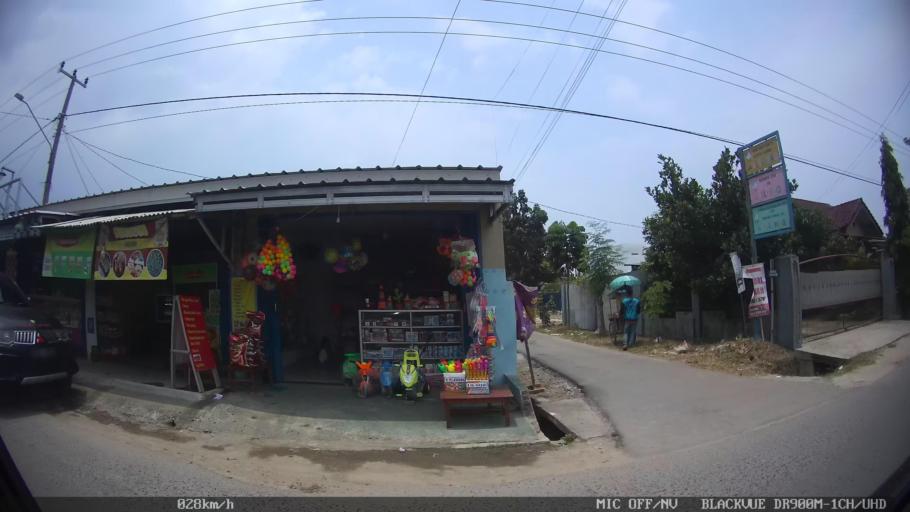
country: ID
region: Lampung
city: Kedaton
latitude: -5.3944
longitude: 105.3050
